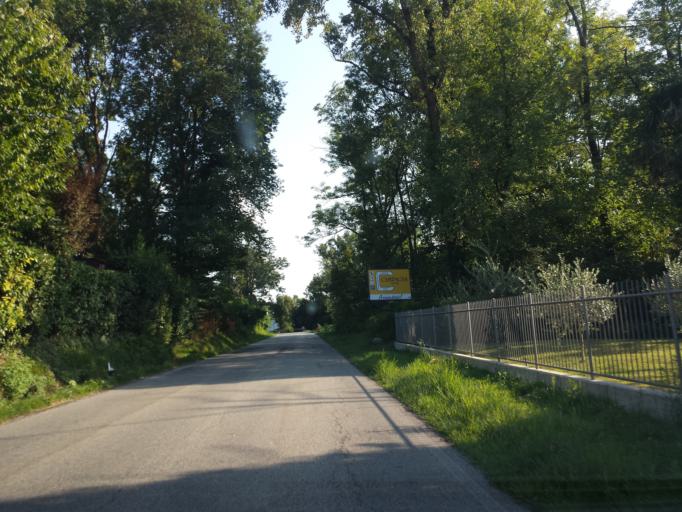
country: IT
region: Lombardy
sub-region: Provincia di Varese
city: Monvalle
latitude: 45.8561
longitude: 8.6133
